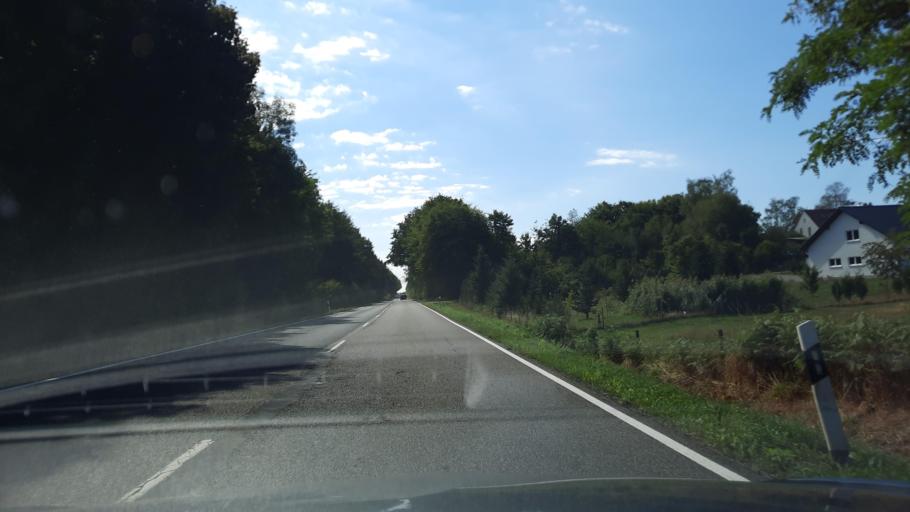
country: DE
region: Rheinland-Pfalz
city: Paschel
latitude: 49.6319
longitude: 6.6640
